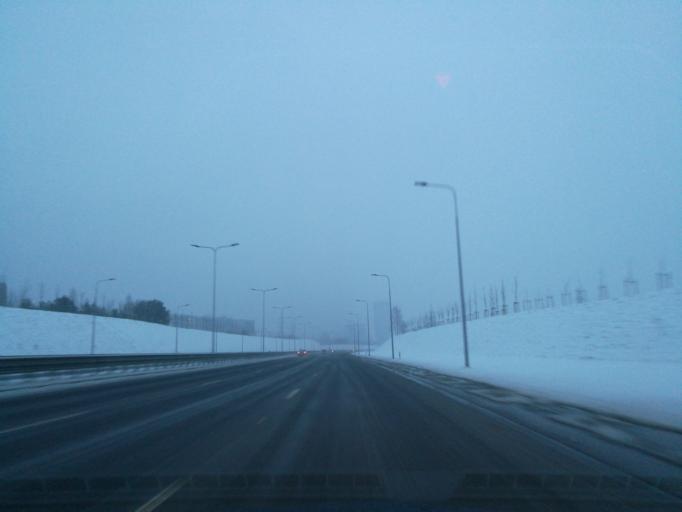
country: LT
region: Vilnius County
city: Justiniskes
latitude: 54.7113
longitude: 25.2086
